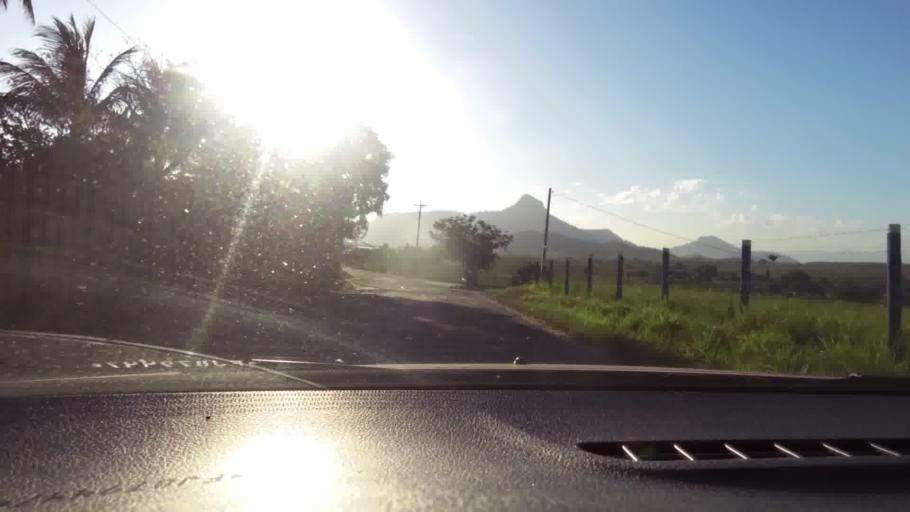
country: BR
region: Espirito Santo
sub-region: Guarapari
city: Guarapari
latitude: -20.5315
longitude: -40.4580
